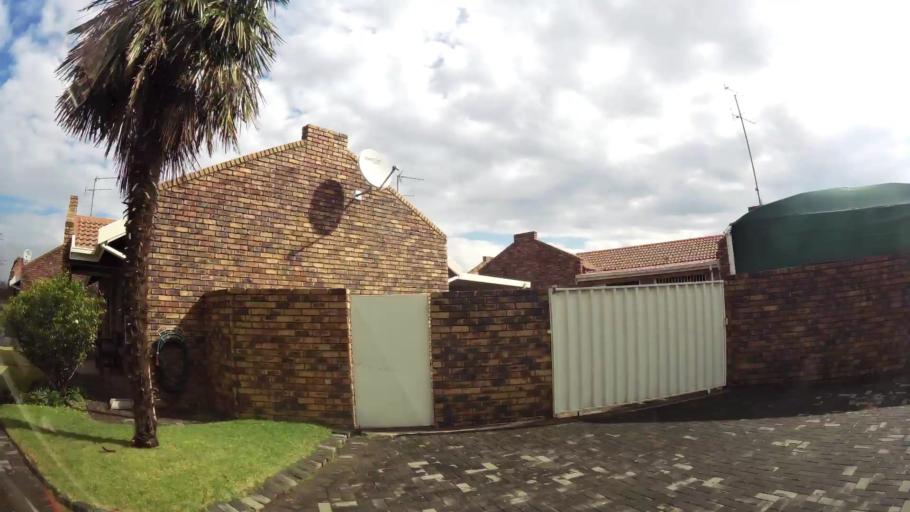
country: ZA
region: Gauteng
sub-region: Sedibeng District Municipality
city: Vereeniging
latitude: -26.6519
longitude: 27.9768
